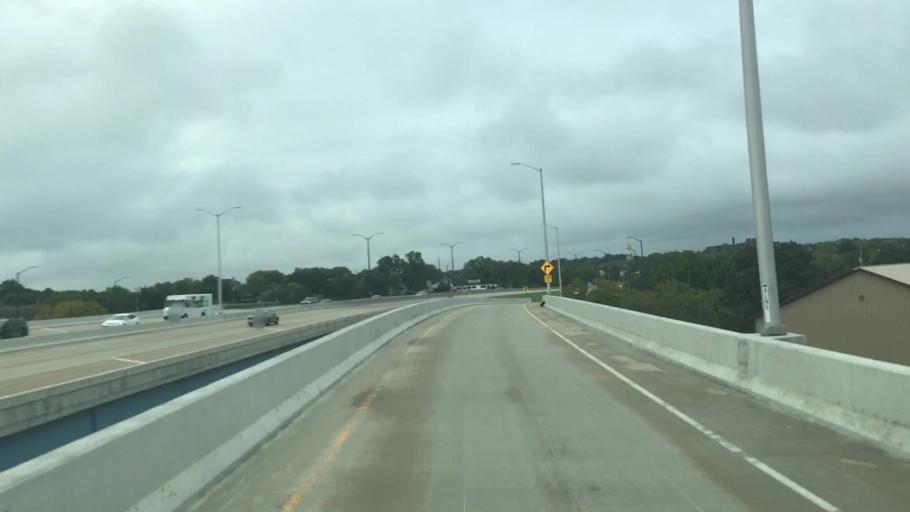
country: US
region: Wisconsin
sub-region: Milwaukee County
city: Milwaukee
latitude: 43.0048
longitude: -87.8922
